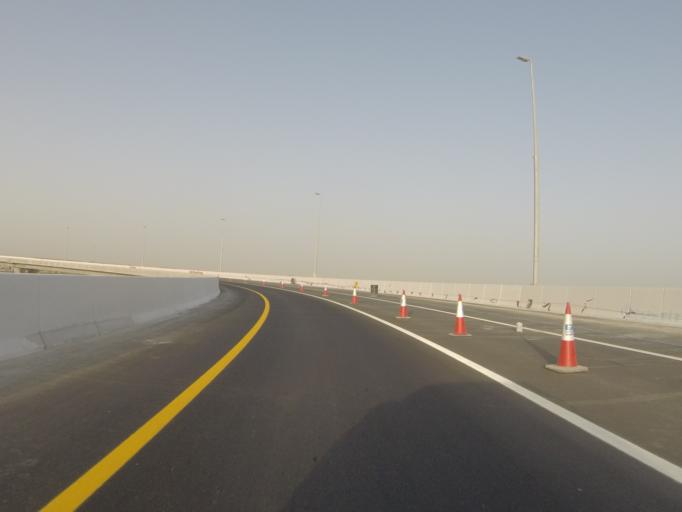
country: AE
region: Dubai
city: Dubai
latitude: 24.9201
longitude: 54.9919
